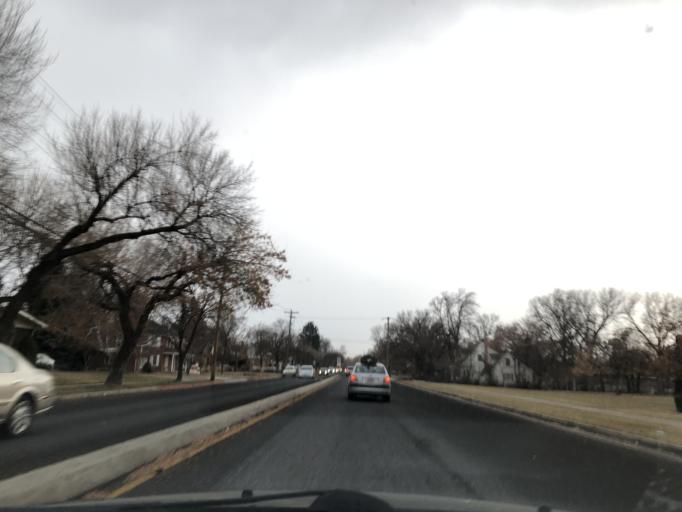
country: US
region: Utah
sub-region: Cache County
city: Logan
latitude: 41.7482
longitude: -111.8294
